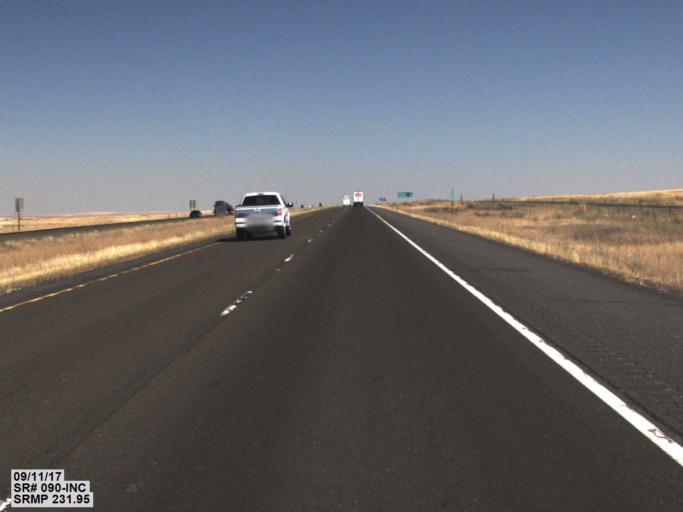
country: US
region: Washington
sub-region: Adams County
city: Ritzville
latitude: 47.2153
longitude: -118.2126
